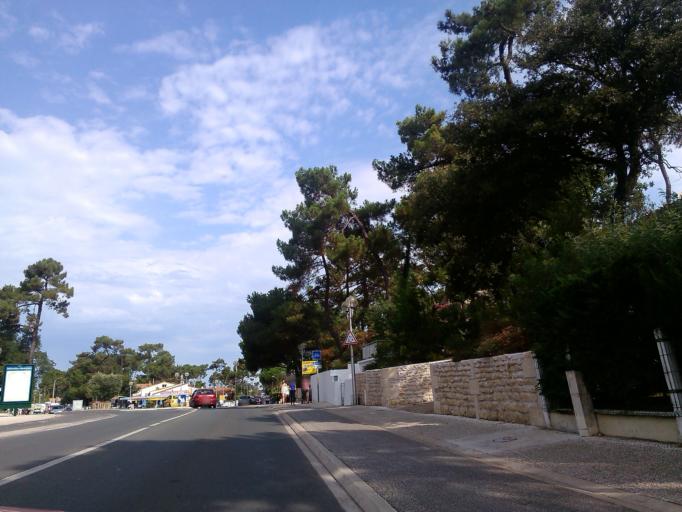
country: FR
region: Poitou-Charentes
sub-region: Departement de la Charente-Maritime
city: La Tremblade
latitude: 45.7919
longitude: -1.1605
